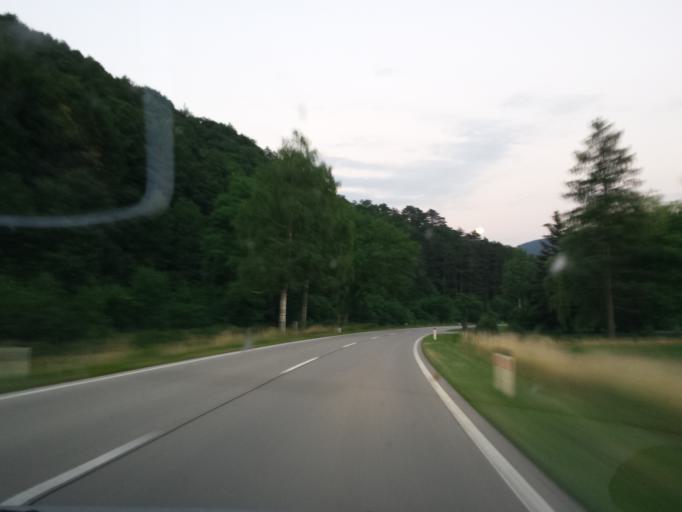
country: AT
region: Lower Austria
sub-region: Politischer Bezirk Baden
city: Altenmarkt an der Triesting
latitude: 48.0239
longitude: 15.9550
